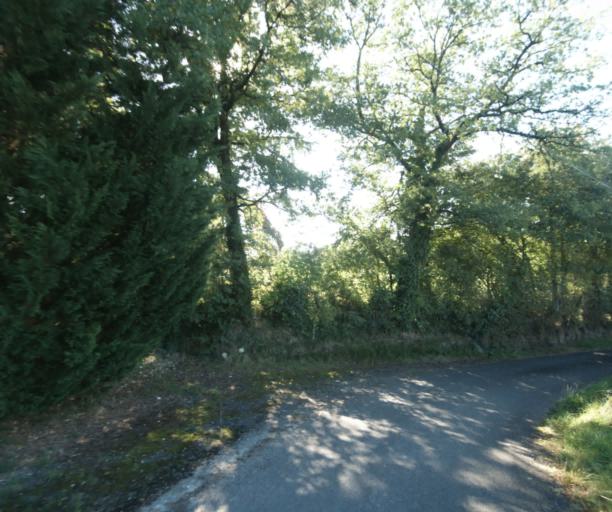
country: FR
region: Midi-Pyrenees
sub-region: Departement du Gers
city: Gondrin
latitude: 43.8255
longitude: 0.2596
